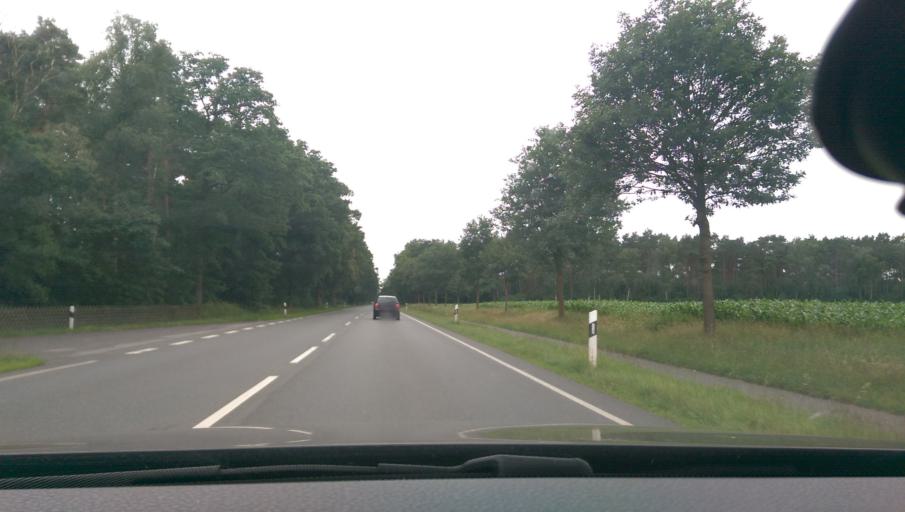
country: DE
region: Lower Saxony
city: Rotenburg
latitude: 53.0930
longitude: 9.3720
